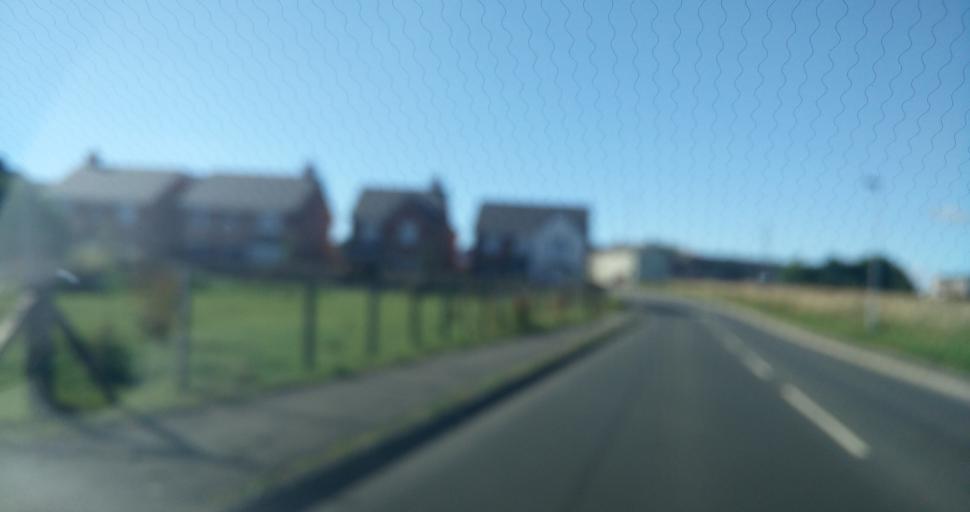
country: GB
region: England
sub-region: County Durham
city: Ushaw Moor
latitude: 54.7446
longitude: -1.6154
